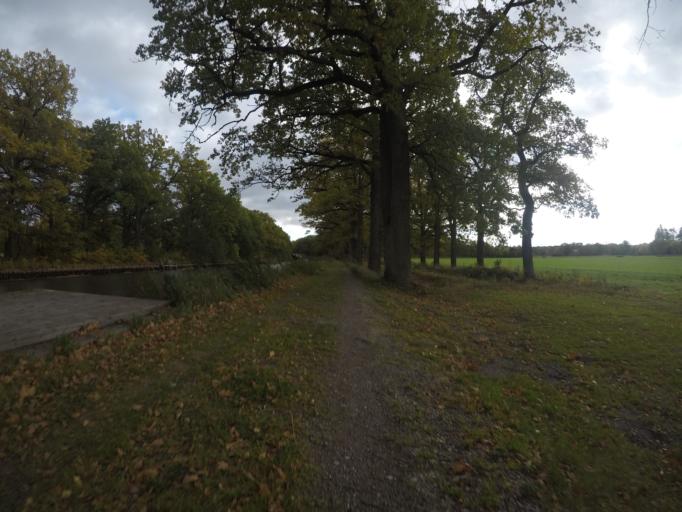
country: SE
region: Vaestmanland
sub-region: Arboga Kommun
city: Tyringe
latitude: 59.3860
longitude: 15.9403
